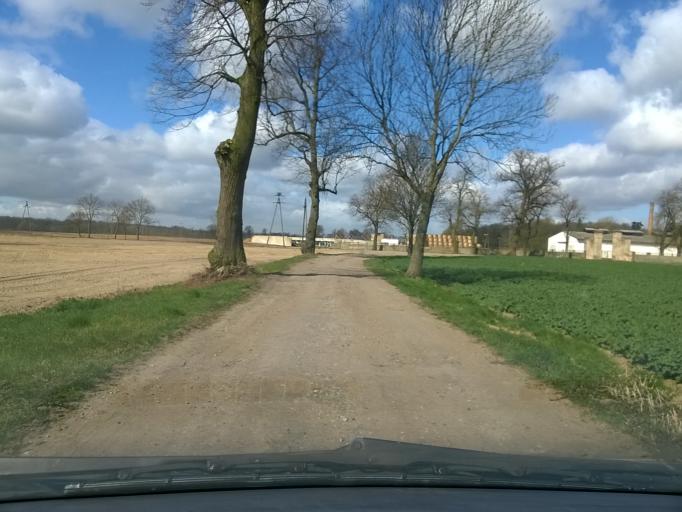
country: PL
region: Kujawsko-Pomorskie
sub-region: Powiat nakielski
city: Kcynia
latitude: 52.9849
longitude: 17.4277
